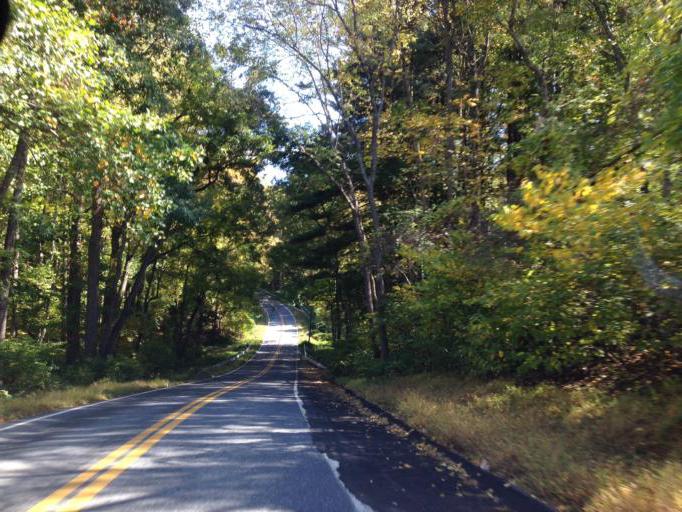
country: US
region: Maryland
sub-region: Howard County
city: Fulton
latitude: 39.1329
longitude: -76.9034
